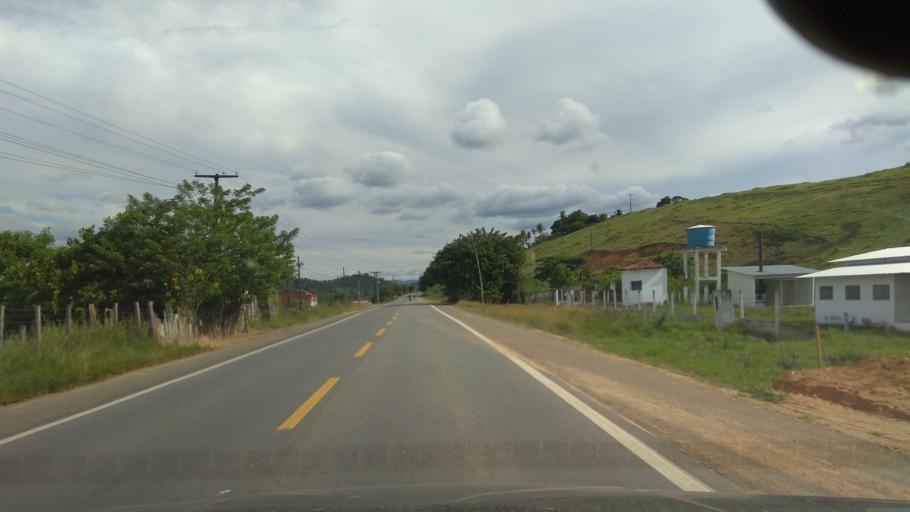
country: BR
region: Bahia
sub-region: Jitauna
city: Jitauna
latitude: -14.0129
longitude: -39.8807
